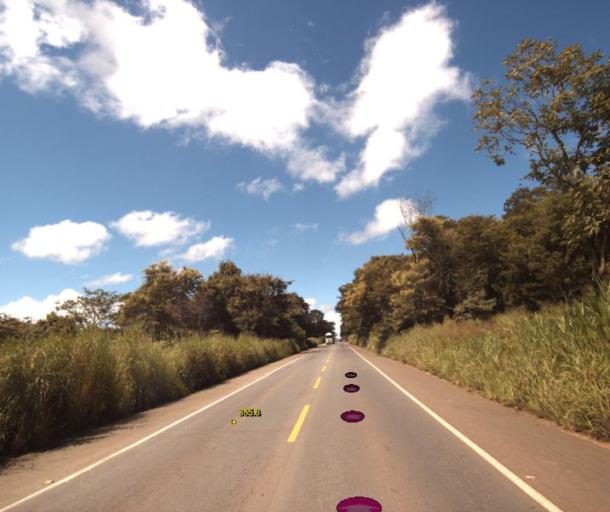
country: BR
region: Goias
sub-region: Jaragua
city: Jaragua
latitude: -15.7892
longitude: -49.3025
